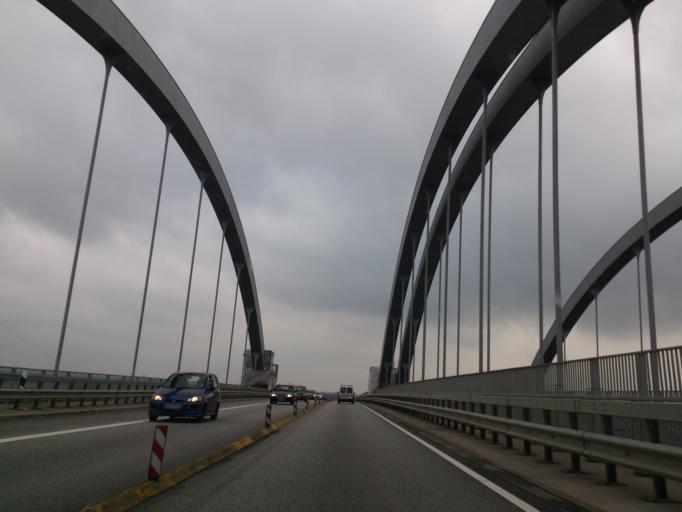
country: DE
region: Schleswig-Holstein
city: Heiligenstedten
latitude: 53.9268
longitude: 9.4799
